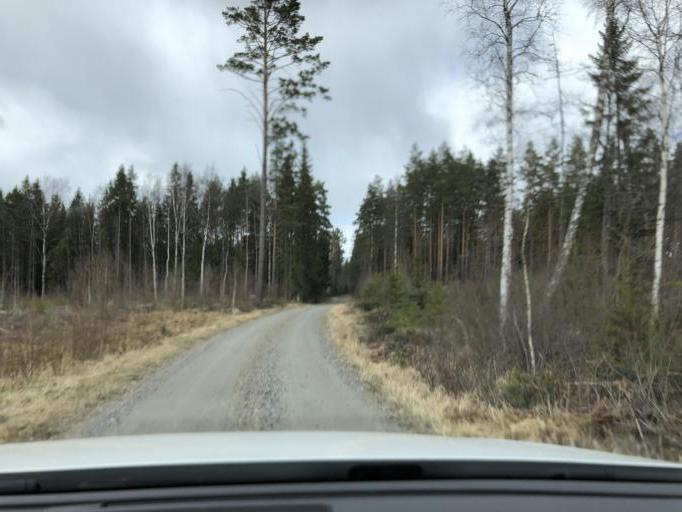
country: SE
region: Gaevleborg
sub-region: Gavle Kommun
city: Hedesunda
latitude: 60.3247
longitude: 17.1049
